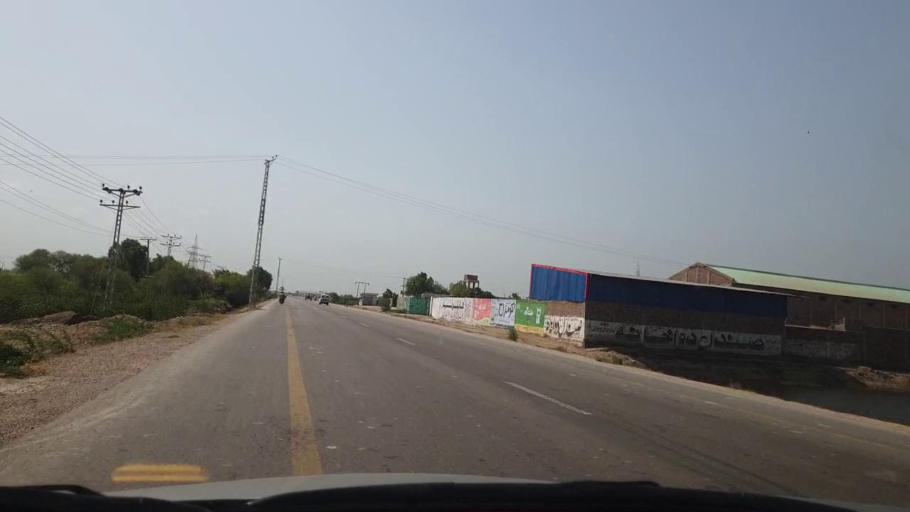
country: PK
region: Sindh
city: Matli
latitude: 25.0125
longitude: 68.6512
